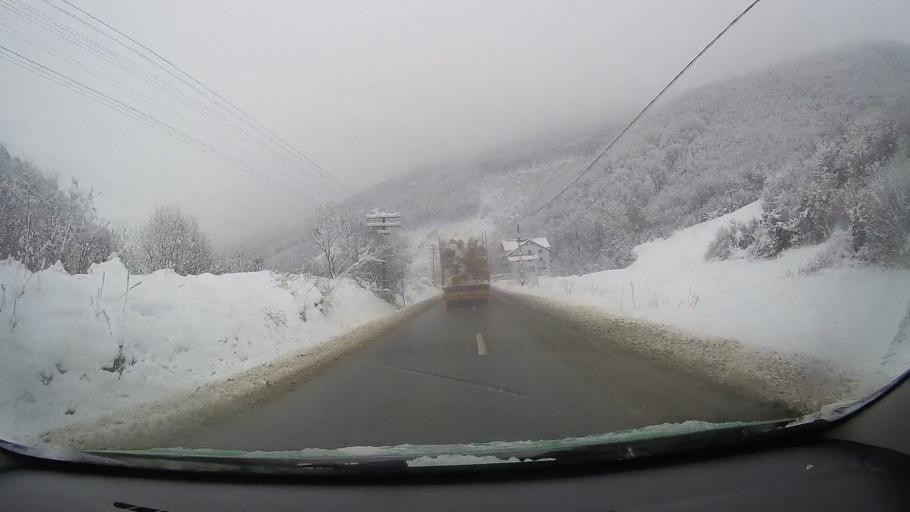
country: RO
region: Sibiu
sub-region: Comuna Orlat
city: Orlat
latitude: 45.7622
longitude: 23.9408
